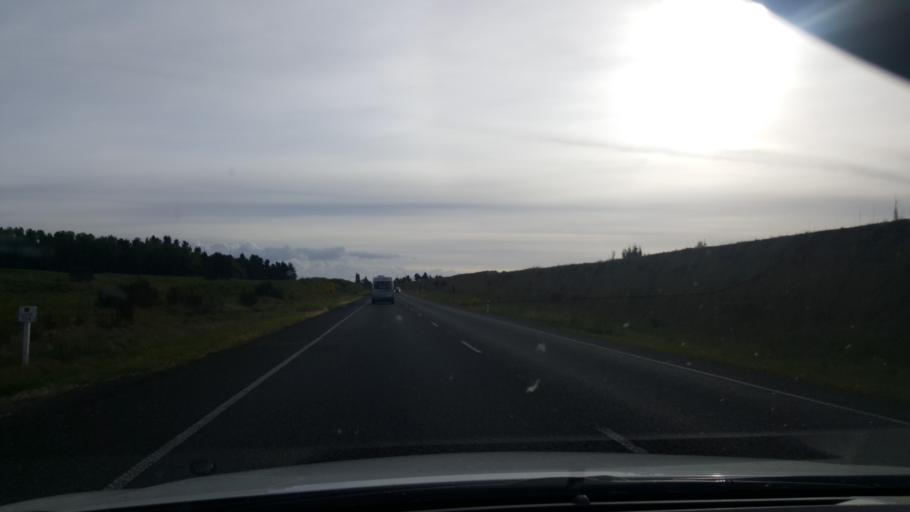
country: NZ
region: Waikato
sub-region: Taupo District
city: Taupo
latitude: -38.7332
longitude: 176.0797
